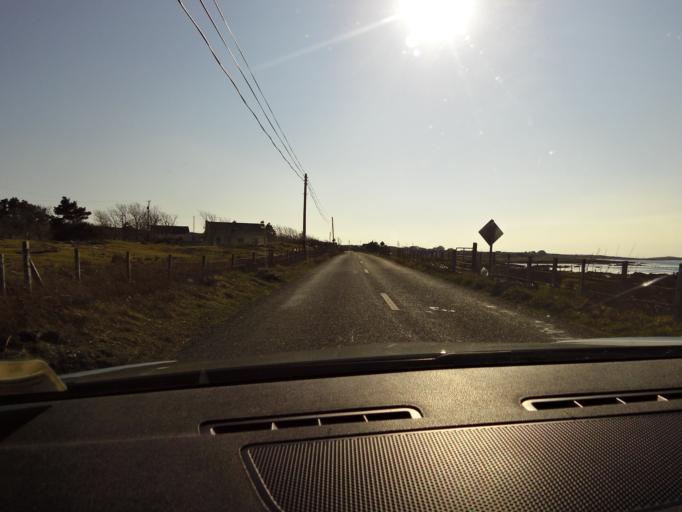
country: IE
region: Connaught
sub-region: County Galway
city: Clifden
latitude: 53.4605
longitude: -10.0329
